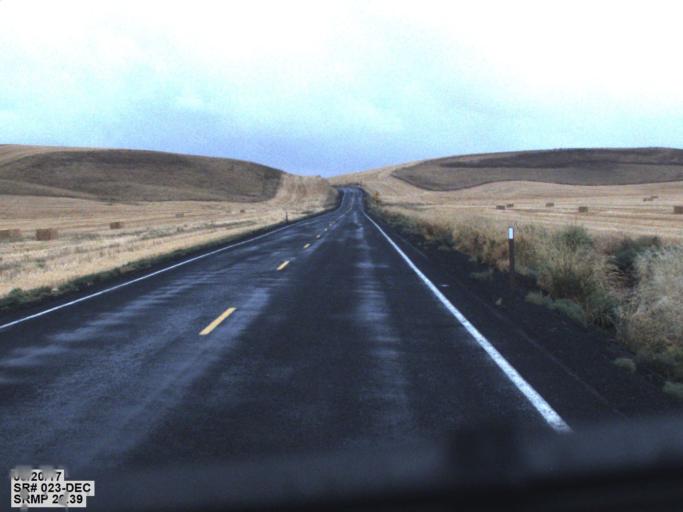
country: US
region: Washington
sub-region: Spokane County
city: Cheney
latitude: 47.1464
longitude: -117.8363
